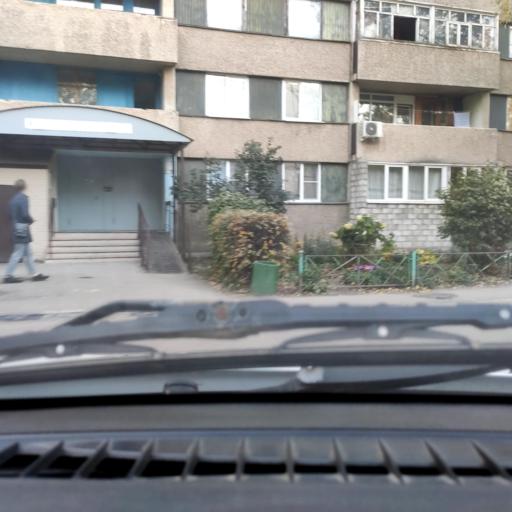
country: RU
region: Samara
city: Tol'yatti
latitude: 53.5334
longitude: 49.3107
